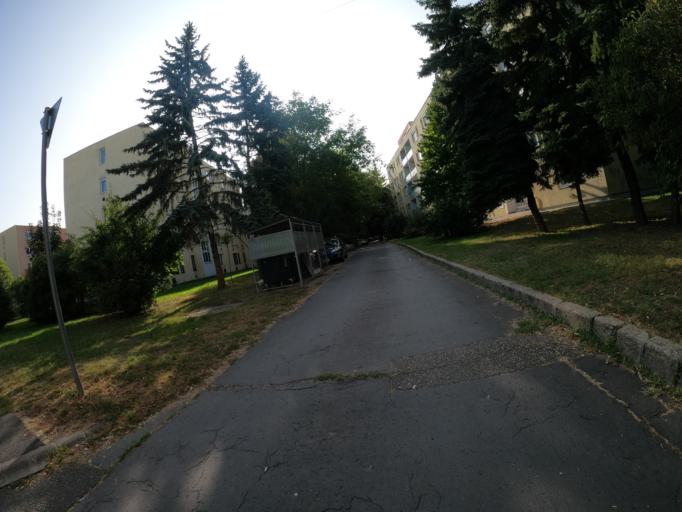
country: HU
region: Borsod-Abauj-Zemplen
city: Sajobabony
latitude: 48.0991
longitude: 20.7081
